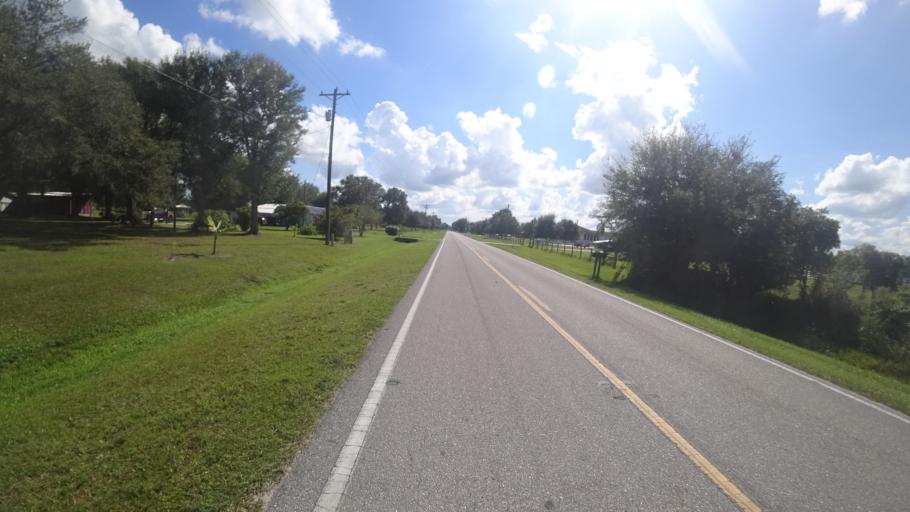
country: US
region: Florida
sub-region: Sarasota County
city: Lake Sarasota
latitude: 27.3604
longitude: -82.1625
